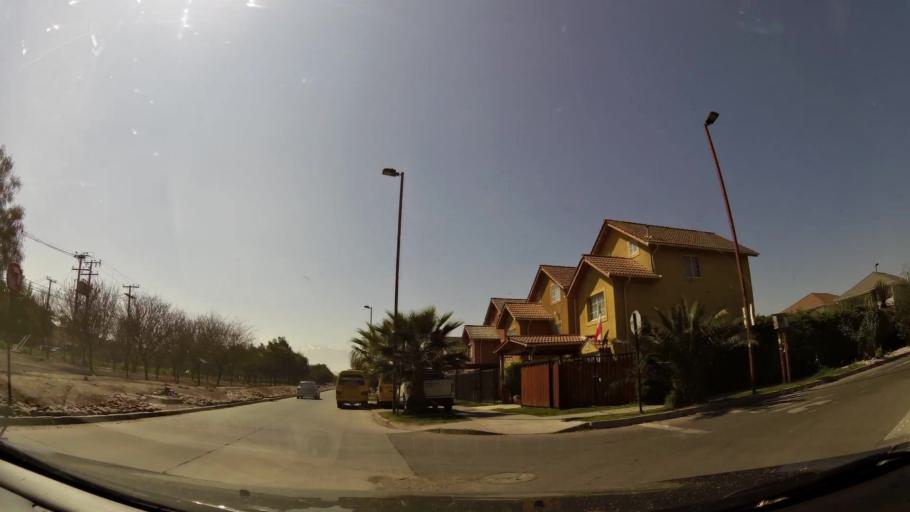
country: CL
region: Santiago Metropolitan
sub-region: Provincia de Chacabuco
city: Chicureo Abajo
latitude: -33.3257
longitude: -70.7495
